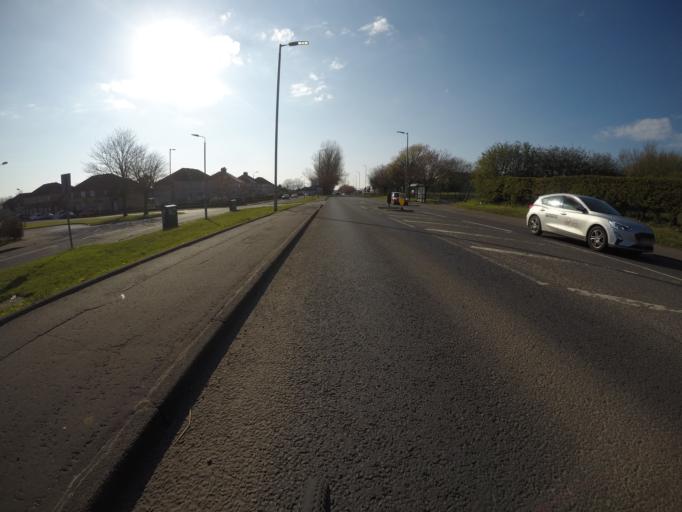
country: GB
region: Scotland
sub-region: North Ayrshire
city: Saltcoats
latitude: 55.6415
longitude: -4.7775
